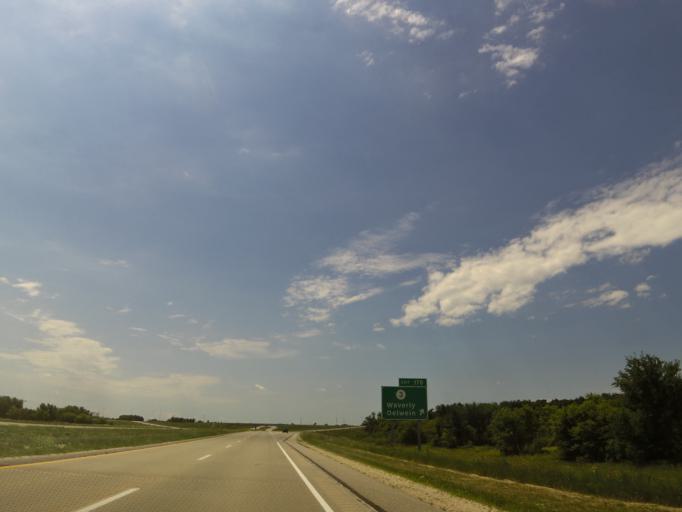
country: US
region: Iowa
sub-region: Bremer County
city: Denver
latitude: 42.7205
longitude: -92.3377
